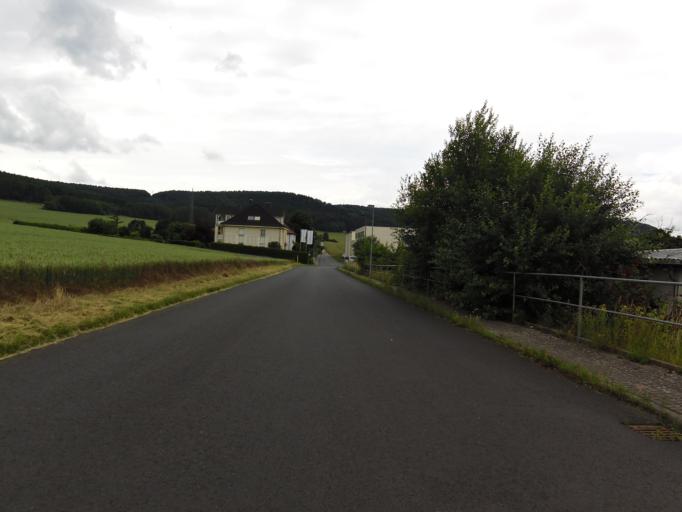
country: DE
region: Thuringia
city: Stadtlengsfeld
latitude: 50.8172
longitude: 10.1241
